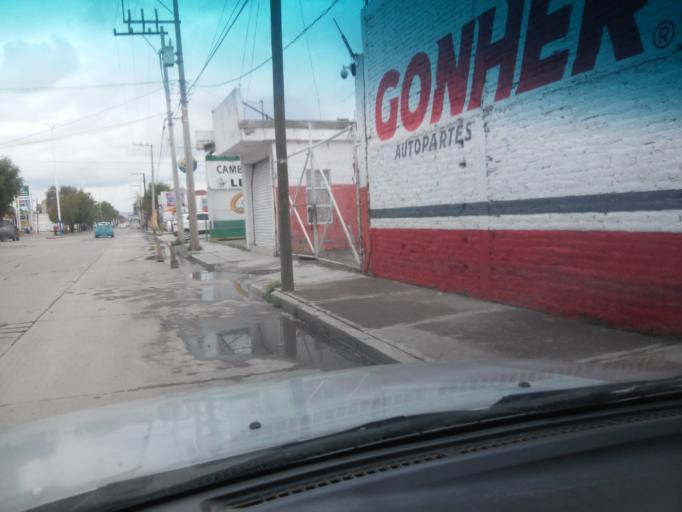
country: MX
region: Durango
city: Victoria de Durango
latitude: 24.0202
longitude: -104.6343
